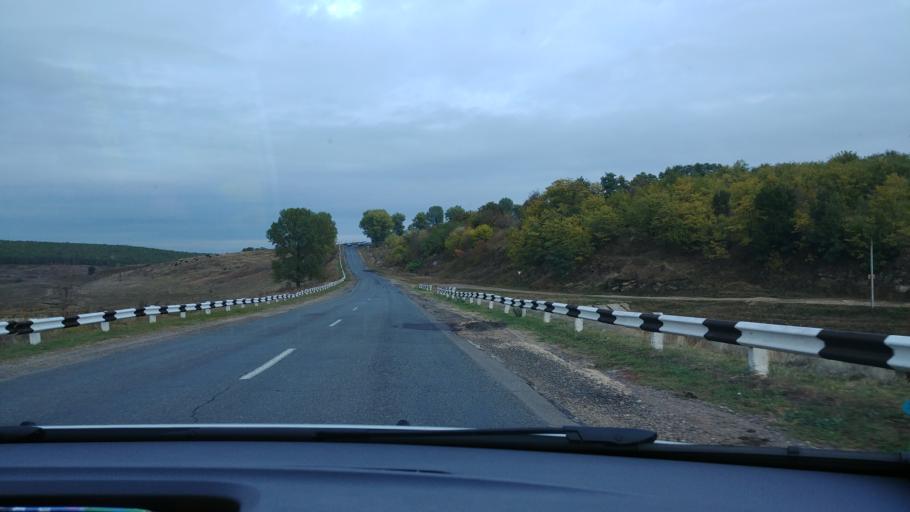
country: MD
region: Rezina
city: Rezina
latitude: 47.7582
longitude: 28.8789
